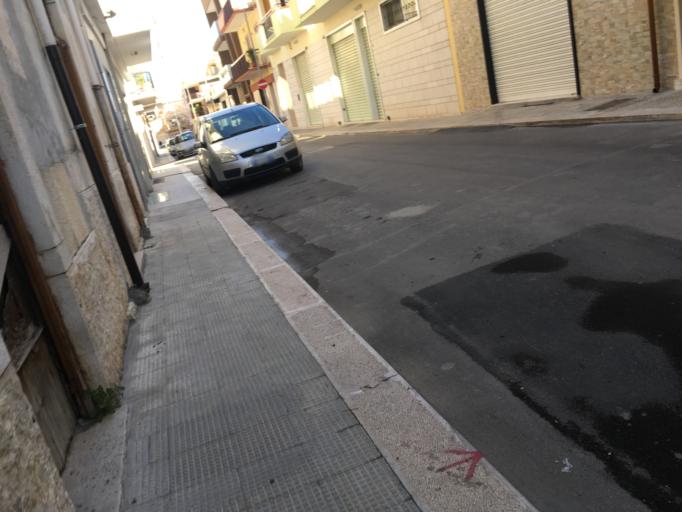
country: IT
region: Apulia
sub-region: Provincia di Barletta - Andria - Trani
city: Andria
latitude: 41.2202
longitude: 16.3052
